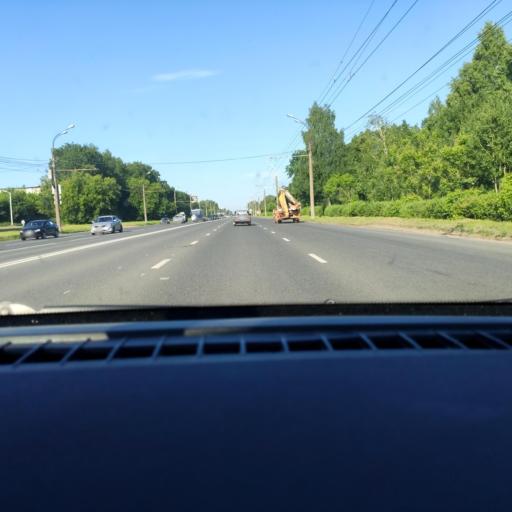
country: RU
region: Udmurtiya
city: Khokhryaki
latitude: 56.8927
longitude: 53.2699
